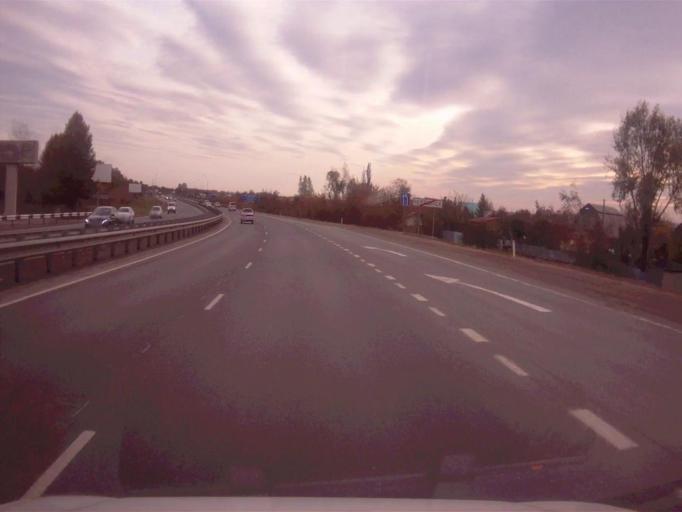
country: RU
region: Chelyabinsk
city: Novosineglazovskiy
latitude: 55.0358
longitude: 61.4419
